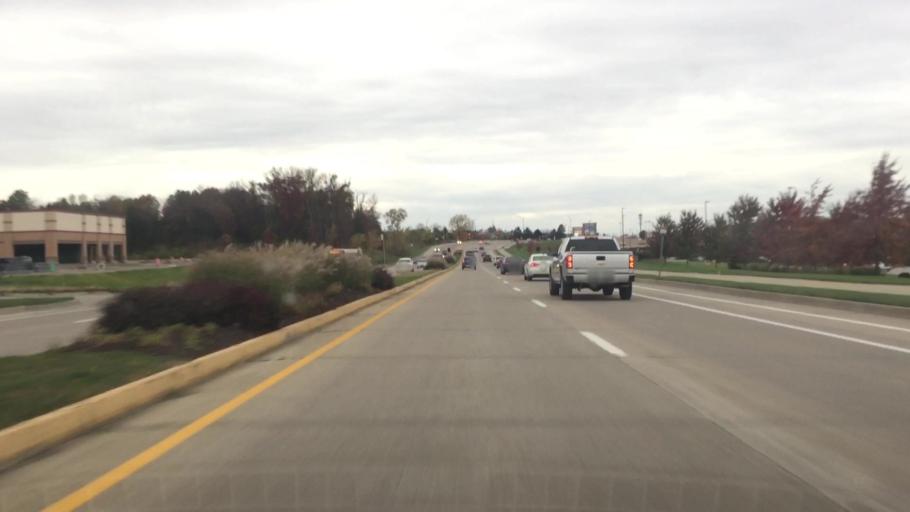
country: US
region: Missouri
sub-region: Boone County
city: Columbia
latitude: 38.9122
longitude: -92.3213
